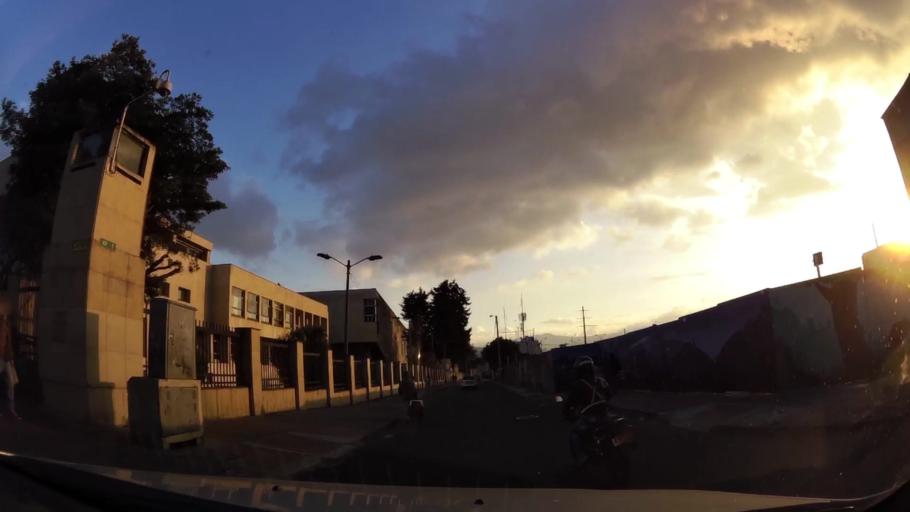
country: CO
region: Bogota D.C.
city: Bogota
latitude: 4.5953
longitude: -74.0796
